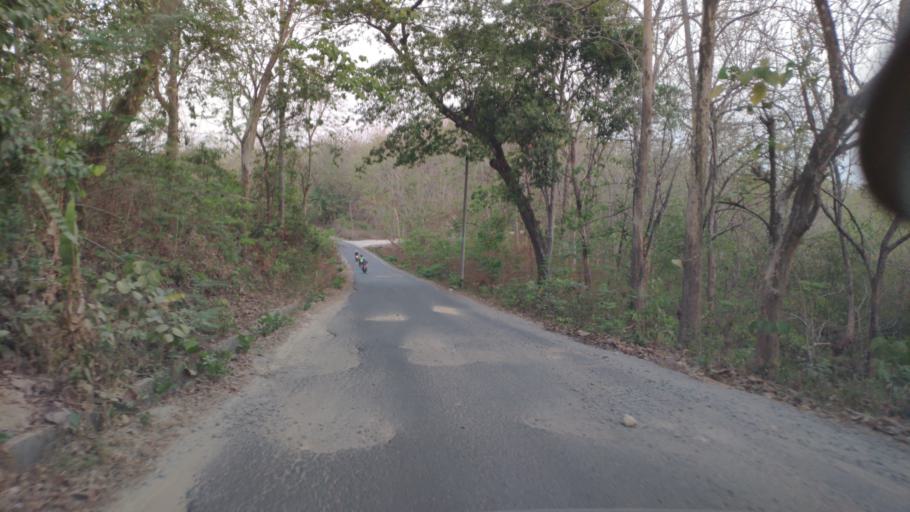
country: ID
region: Central Java
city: Semanggi
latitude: -7.0760
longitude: 111.4170
